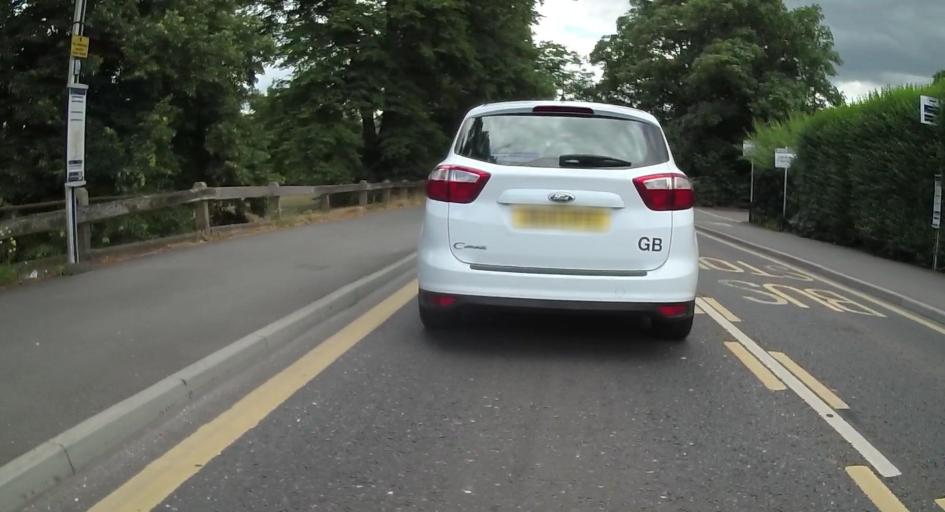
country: GB
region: England
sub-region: Hampshire
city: Aldershot
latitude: 51.2525
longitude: -0.7675
